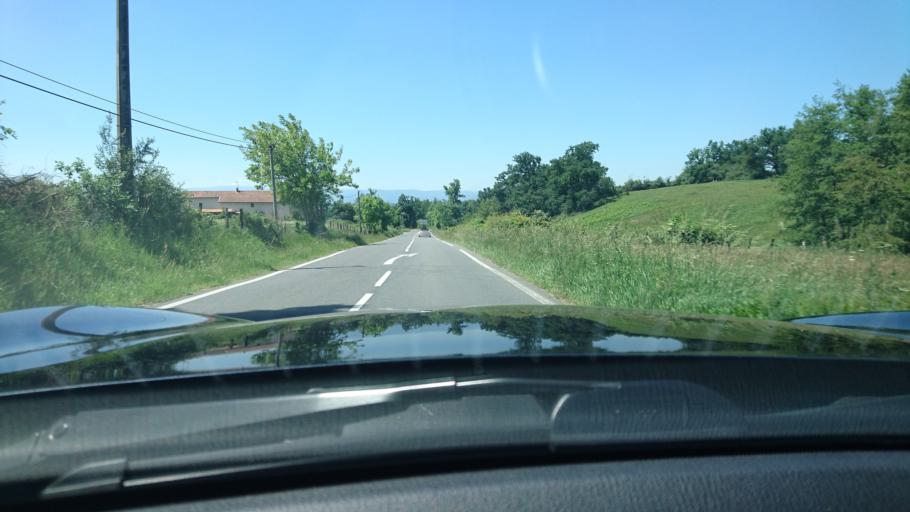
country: FR
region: Rhone-Alpes
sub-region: Departement de la Loire
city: Civens
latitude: 45.7794
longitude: 4.2600
